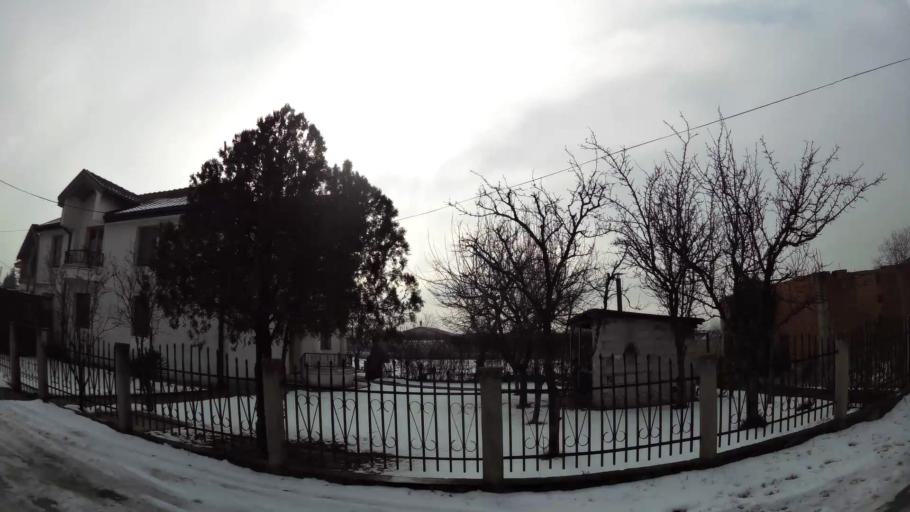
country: MK
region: Ilinden
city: Ilinden
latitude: 41.9895
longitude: 21.5827
